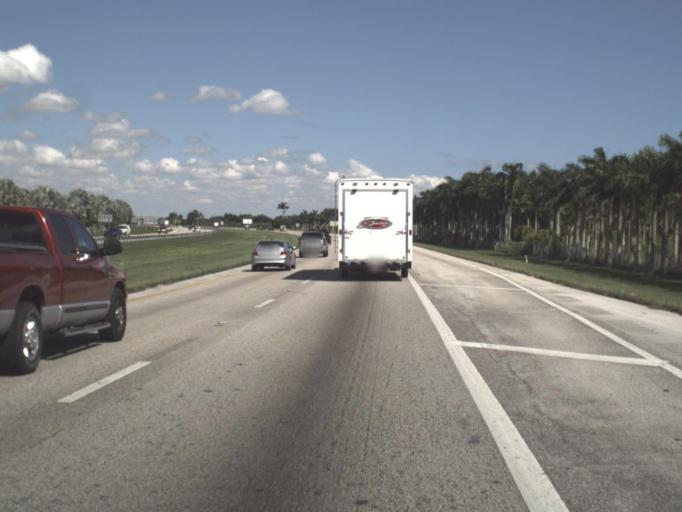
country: US
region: Florida
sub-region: Miami-Dade County
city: Goulds
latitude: 25.5395
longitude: -80.3642
